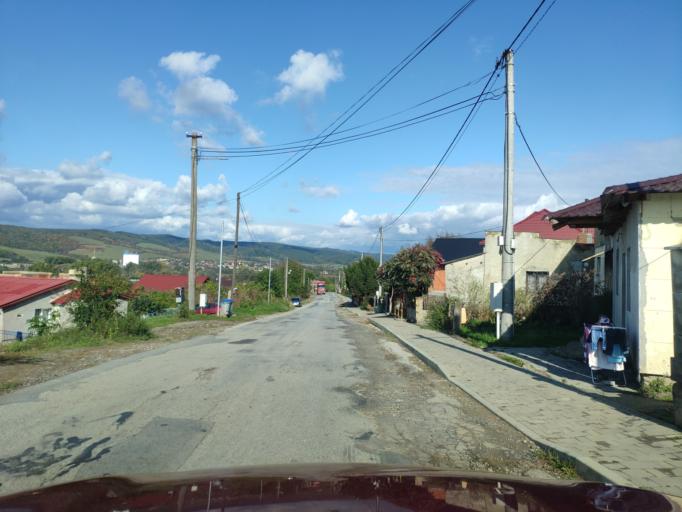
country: SK
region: Presovsky
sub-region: Okres Presov
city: Presov
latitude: 48.9085
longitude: 21.2612
